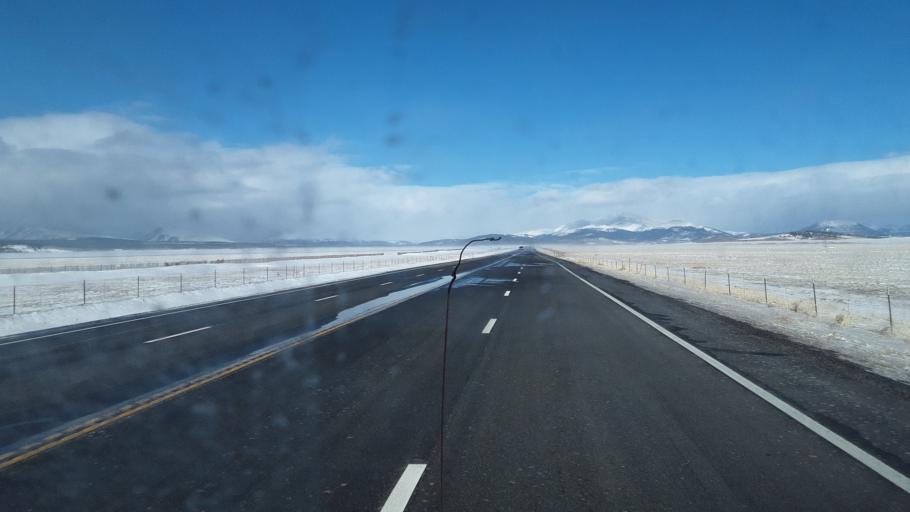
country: US
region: Colorado
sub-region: Park County
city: Fairplay
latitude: 39.1470
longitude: -105.9981
